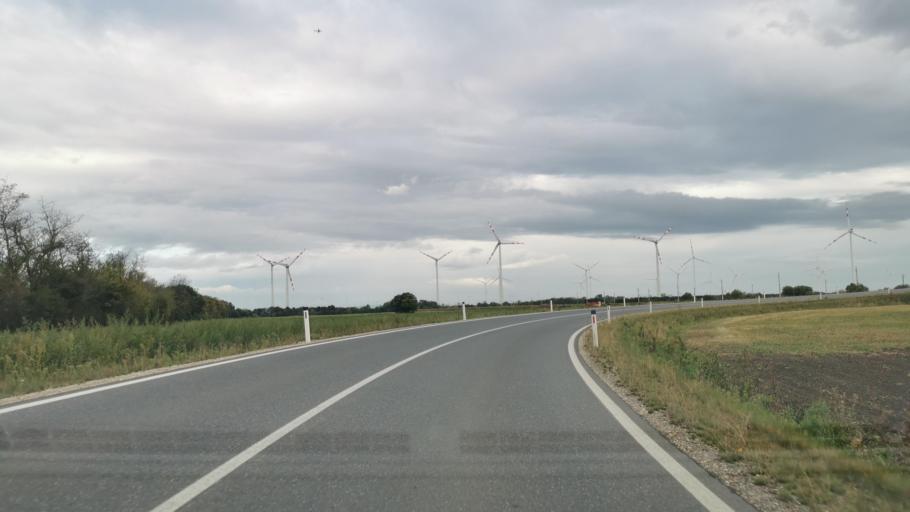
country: AT
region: Lower Austria
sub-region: Politischer Bezirk Ganserndorf
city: Leopoldsdorf im Marchfelde
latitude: 48.2424
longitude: 16.6968
